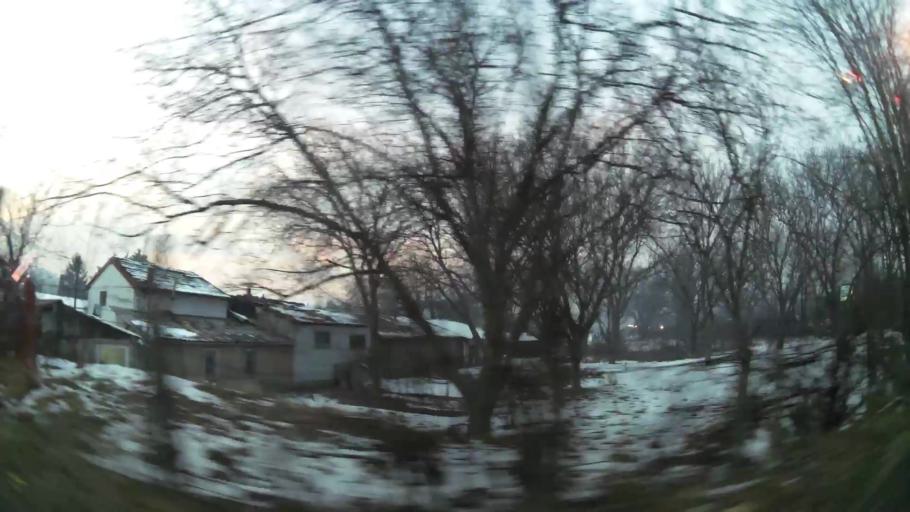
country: MK
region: Suto Orizari
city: Suto Orizare
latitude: 42.0159
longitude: 21.4109
